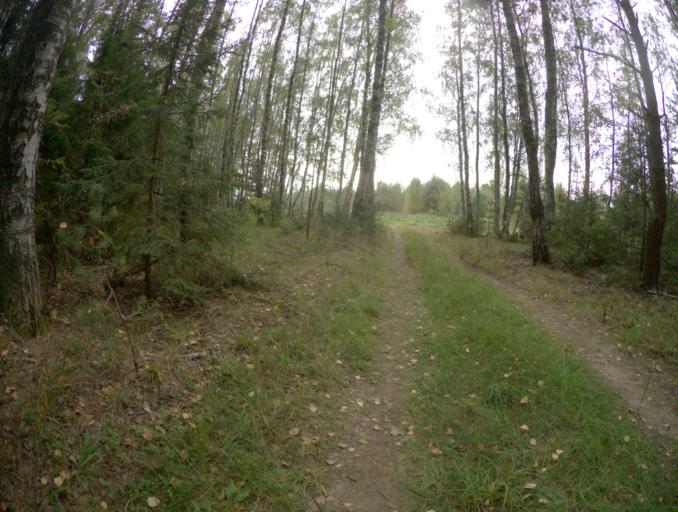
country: RU
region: Vladimir
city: Golovino
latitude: 55.9887
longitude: 40.4634
